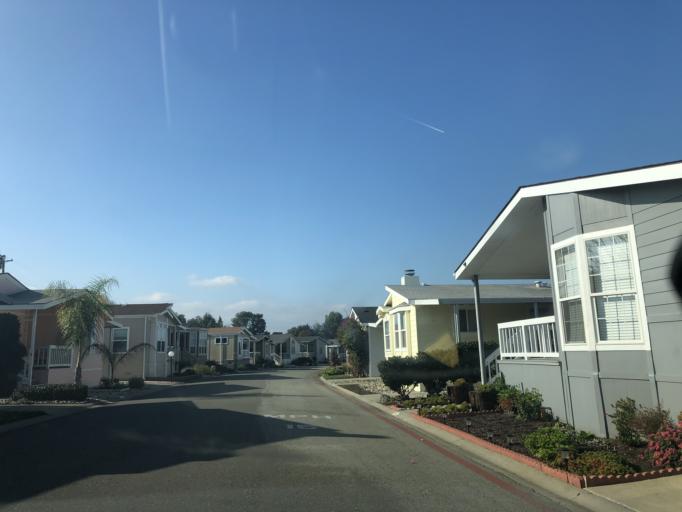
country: US
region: California
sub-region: Santa Clara County
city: Sunnyvale
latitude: 37.4001
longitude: -121.9929
